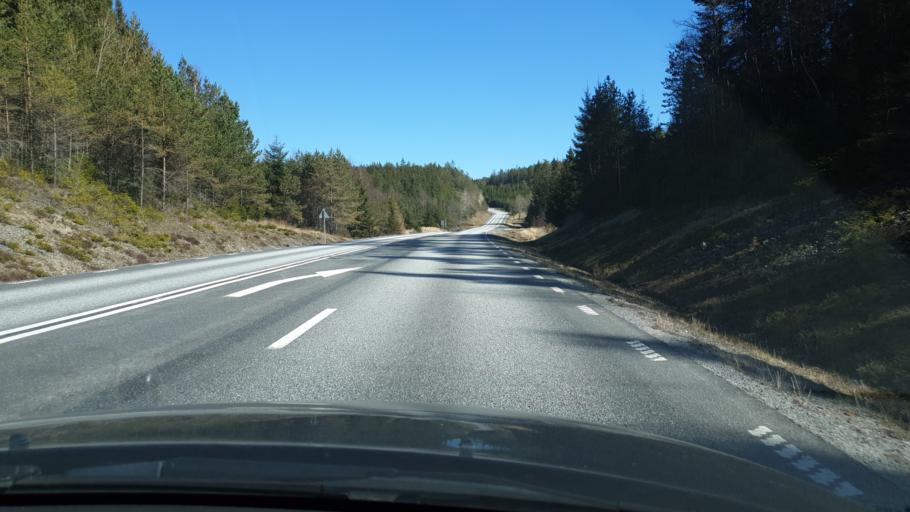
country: SE
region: Vaestra Goetaland
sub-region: Tanums Kommun
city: Tanumshede
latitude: 58.7963
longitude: 11.5845
